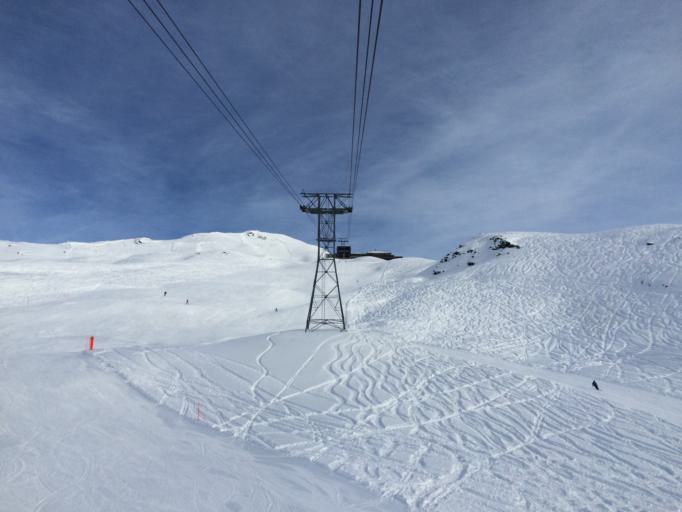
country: CH
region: Grisons
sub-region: Praettigau/Davos District
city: Davos
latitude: 46.8072
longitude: 9.9113
